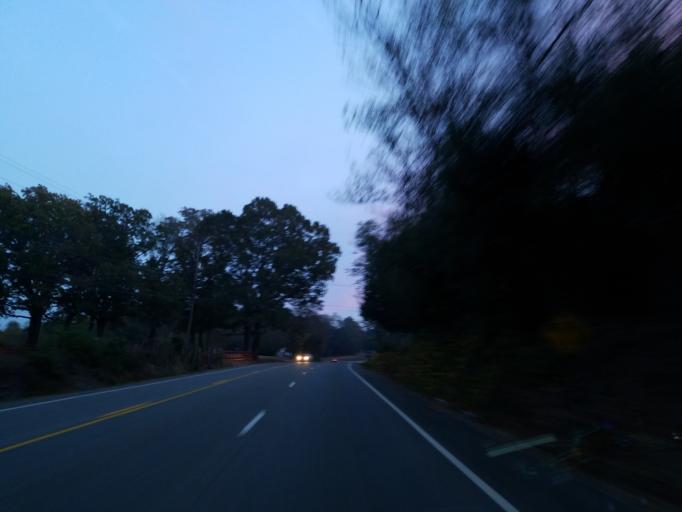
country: US
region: Georgia
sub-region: Pickens County
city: Jasper
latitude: 34.4955
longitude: -84.4699
